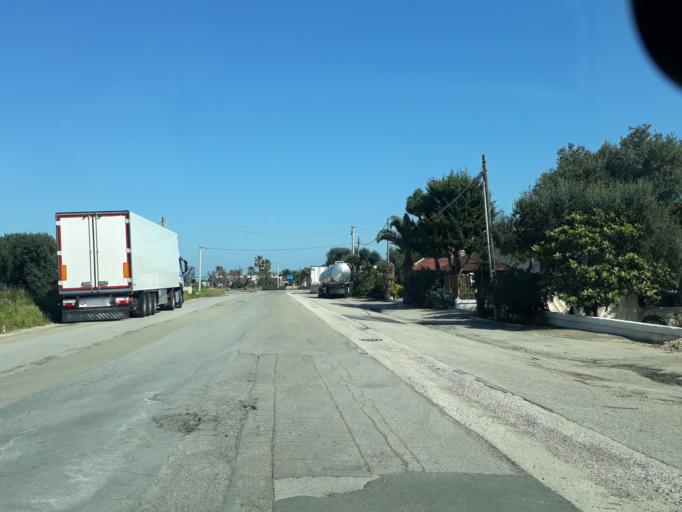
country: IT
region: Apulia
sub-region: Provincia di Brindisi
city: Fasano
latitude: 40.8521
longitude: 17.3511
